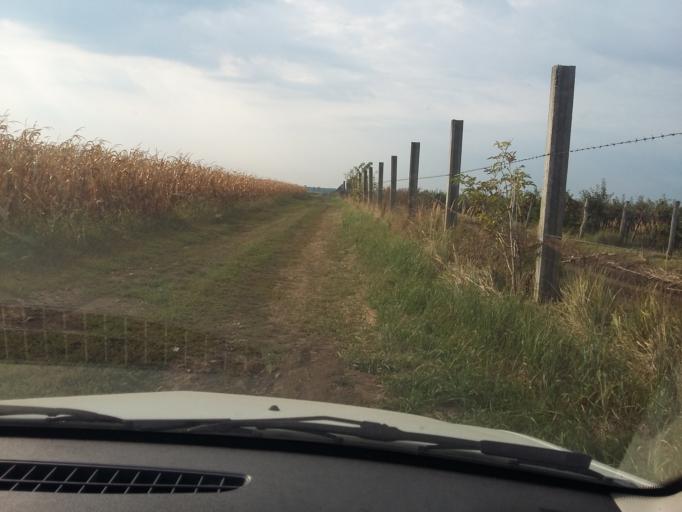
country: HU
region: Borsod-Abauj-Zemplen
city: Taktaharkany
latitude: 48.1343
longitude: 21.1066
